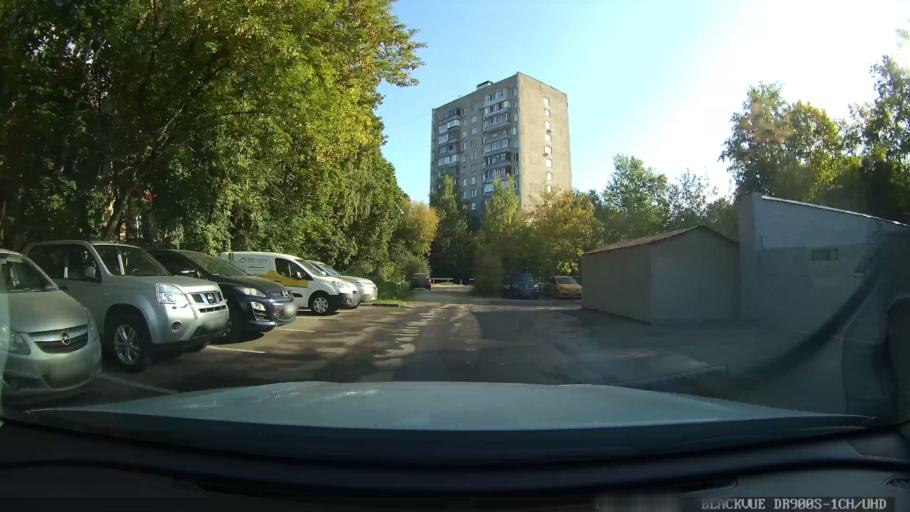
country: RU
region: Moskovskaya
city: Bol'shaya Setun'
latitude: 55.7379
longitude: 37.3988
